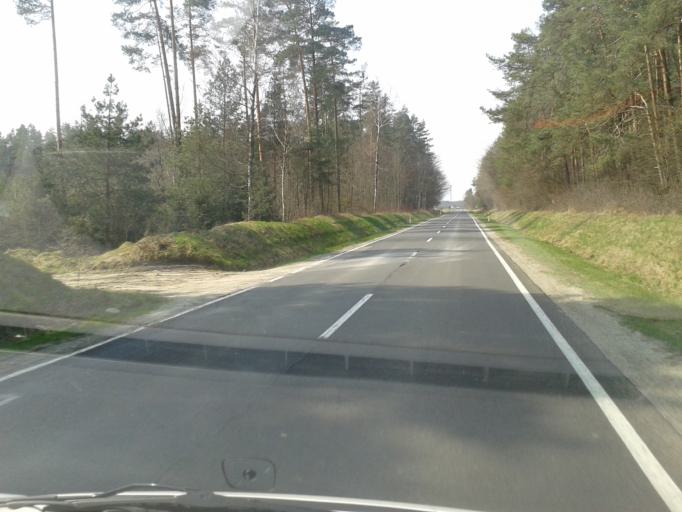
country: PL
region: Subcarpathian Voivodeship
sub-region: Powiat lubaczowski
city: Narol
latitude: 50.3180
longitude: 23.2577
